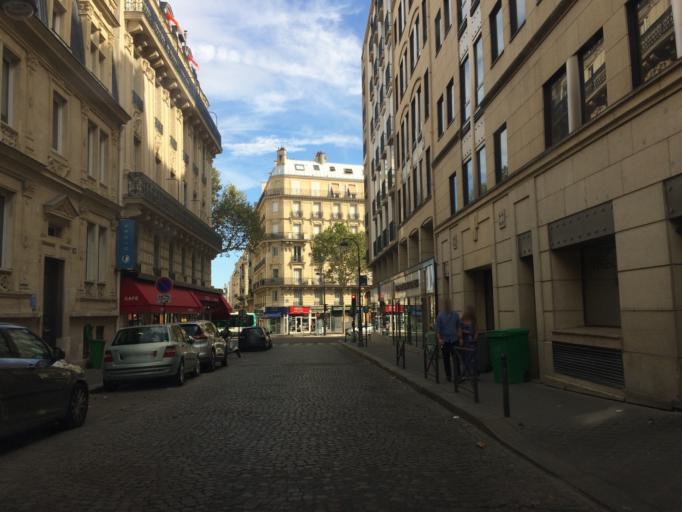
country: FR
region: Ile-de-France
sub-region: Departement des Hauts-de-Seine
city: Neuilly-sur-Seine
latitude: 48.8672
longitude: 2.2892
